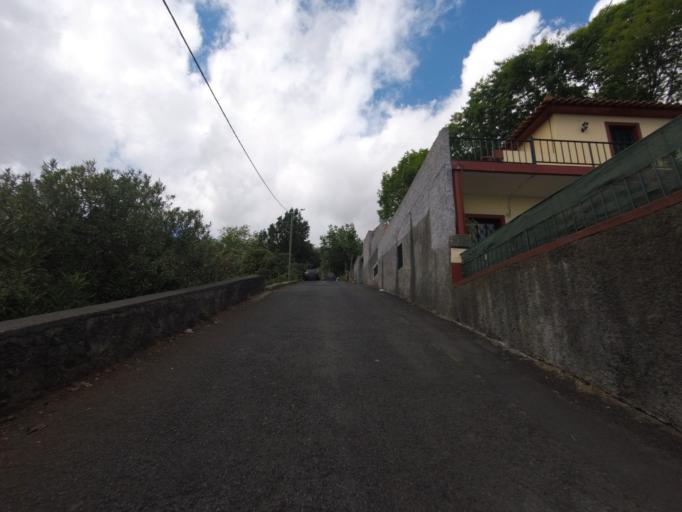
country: PT
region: Madeira
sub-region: Funchal
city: Nossa Senhora do Monte
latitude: 32.6744
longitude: -16.9039
